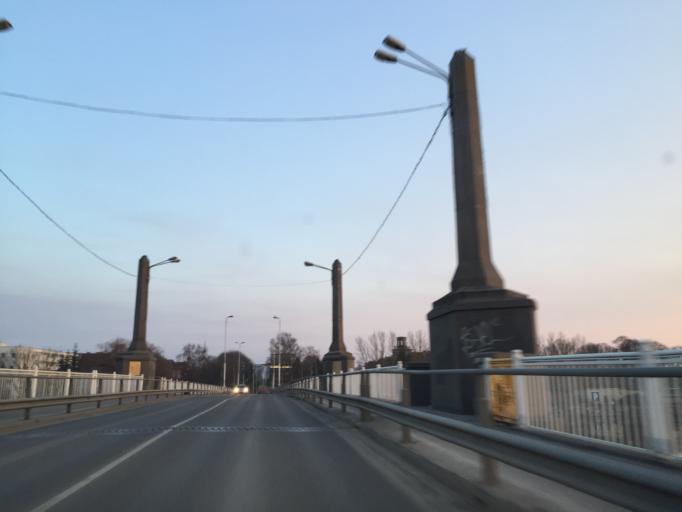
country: EE
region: Paernumaa
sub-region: Paernu linn
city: Parnu
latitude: 58.3892
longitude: 24.4958
